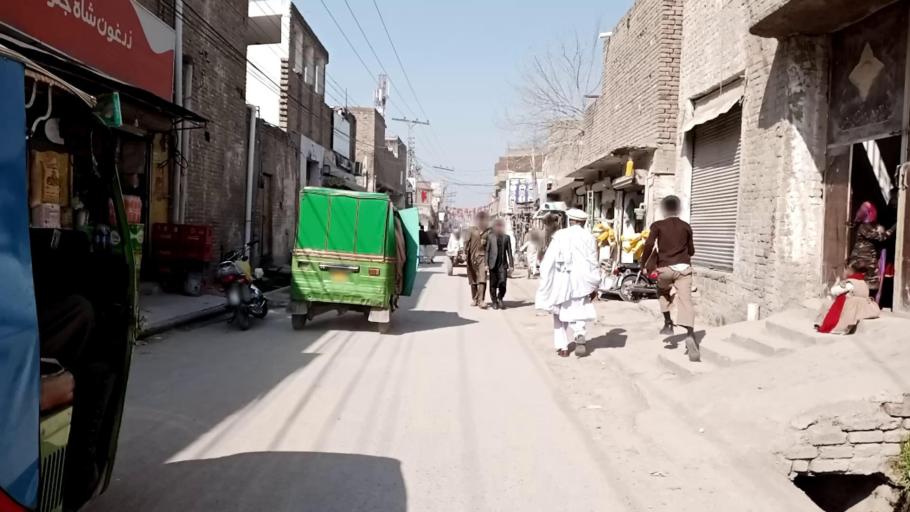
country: PK
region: Khyber Pakhtunkhwa
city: Peshawar
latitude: 34.0108
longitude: 71.5166
